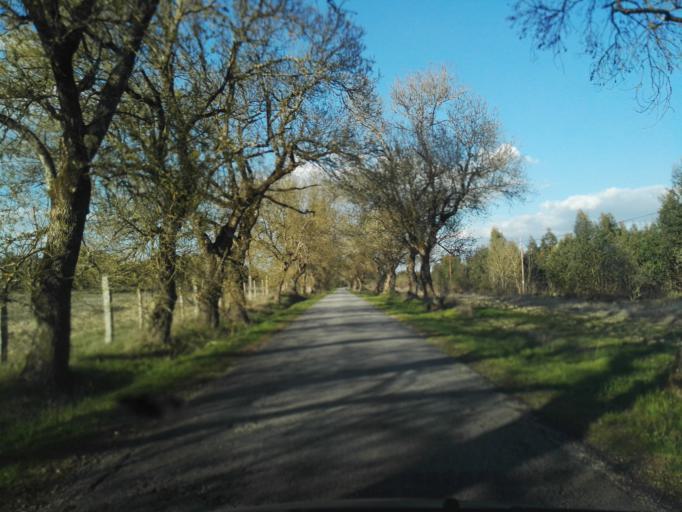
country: PT
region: Evora
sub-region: Evora
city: Evora
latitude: 38.5419
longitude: -7.9379
